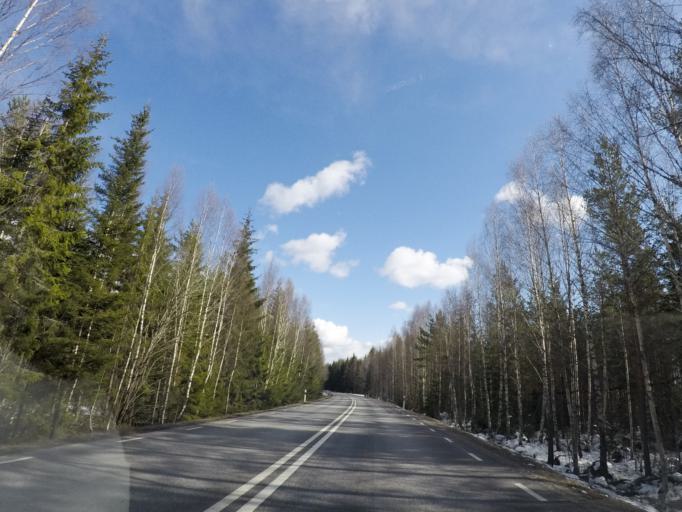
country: SE
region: Vaestmanland
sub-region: Skinnskattebergs Kommun
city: Skinnskatteberg
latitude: 59.8488
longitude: 15.6668
